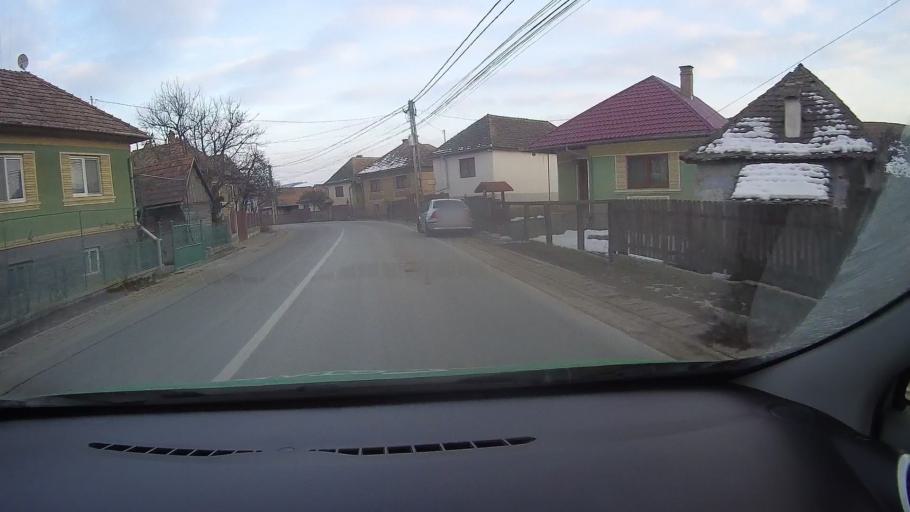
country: RO
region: Harghita
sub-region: Comuna Simonesti
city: Simonesti
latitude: 46.3568
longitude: 25.1450
